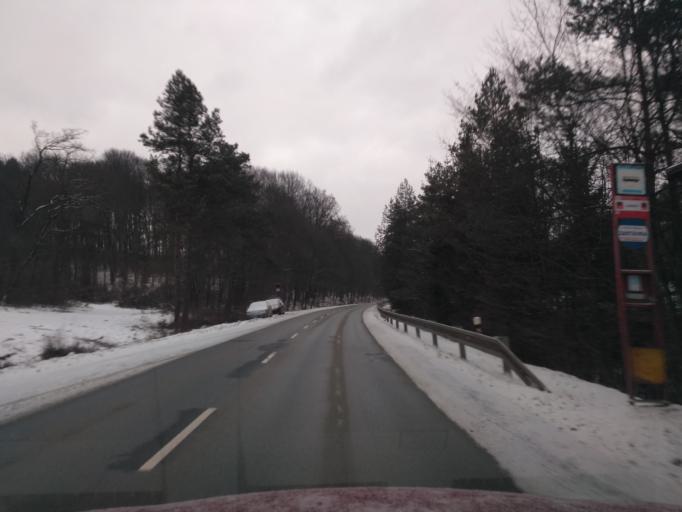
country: SK
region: Presovsky
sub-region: Okres Presov
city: Presov
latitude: 48.9761
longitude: 21.1714
